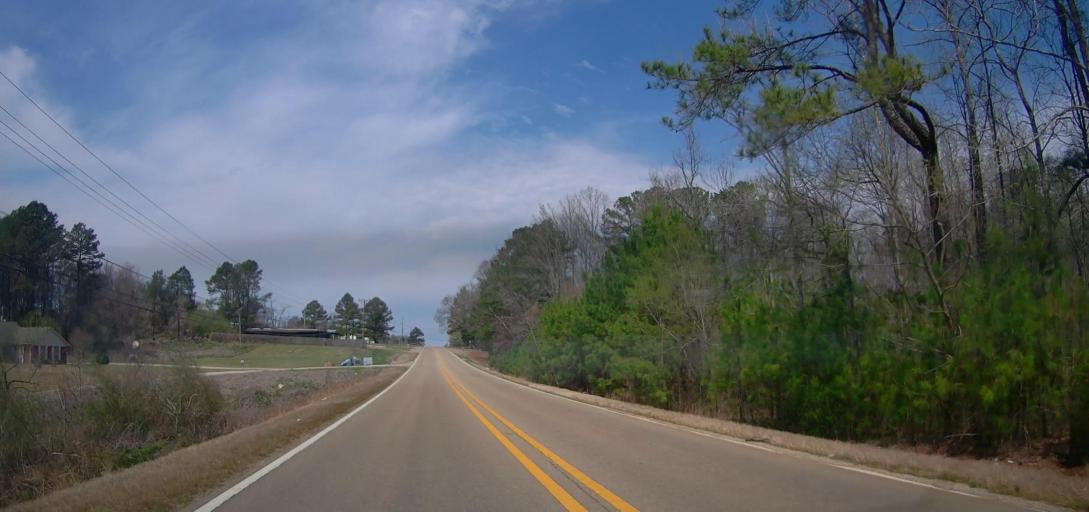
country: US
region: Mississippi
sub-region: Union County
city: New Albany
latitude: 34.4508
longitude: -88.9709
